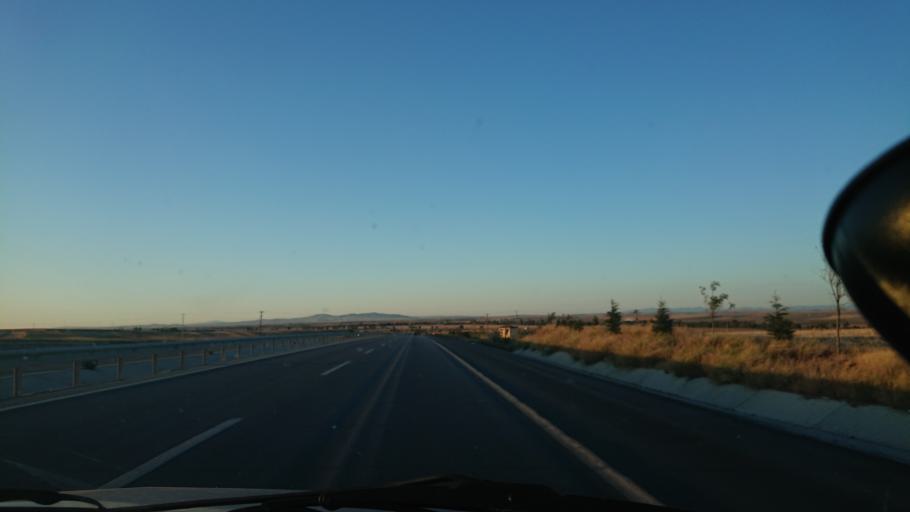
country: TR
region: Eskisehir
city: Mahmudiye
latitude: 39.5088
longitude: 30.9651
